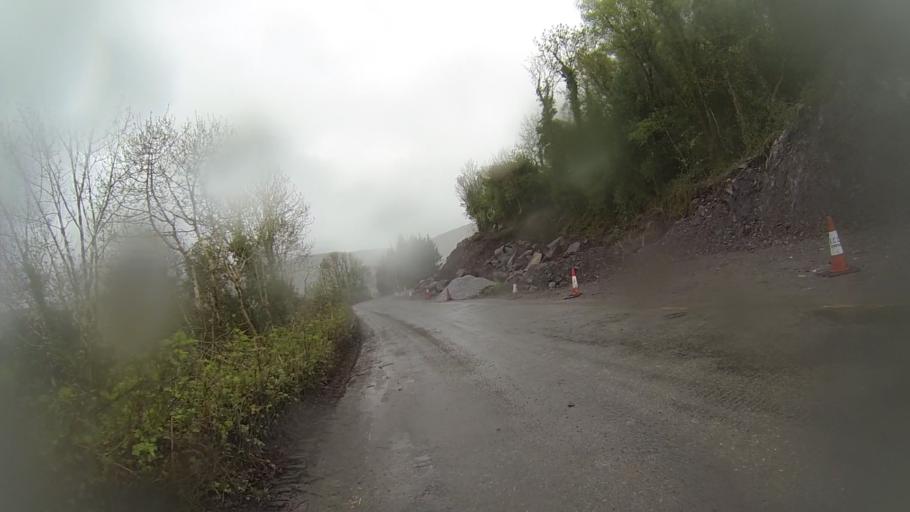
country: IE
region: Munster
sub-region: Ciarrai
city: Kenmare
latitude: 51.8051
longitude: -9.5569
